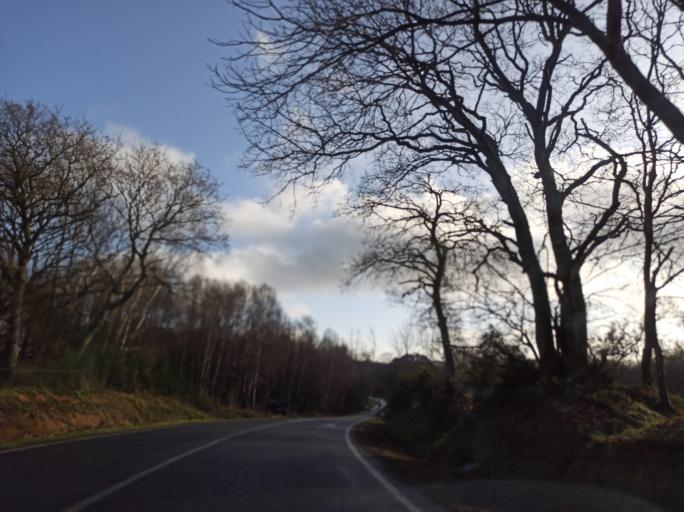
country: ES
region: Galicia
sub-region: Provincia da Coruna
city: Curtis
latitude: 43.0967
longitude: -7.9909
